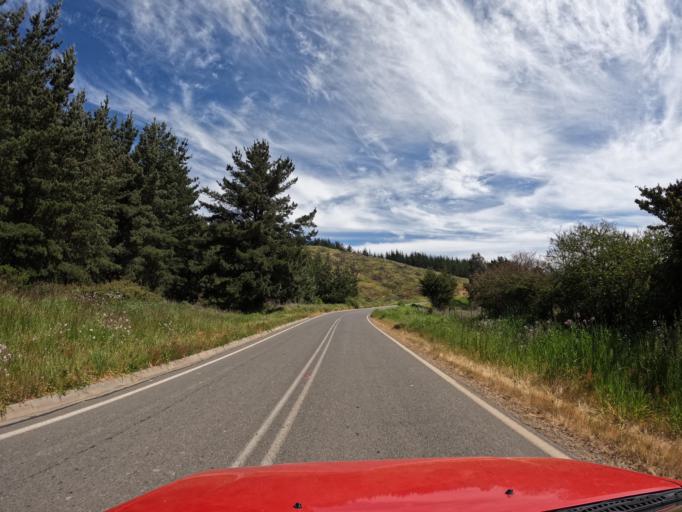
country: CL
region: Maule
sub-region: Provincia de Talca
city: Constitucion
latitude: -35.0382
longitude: -72.0575
